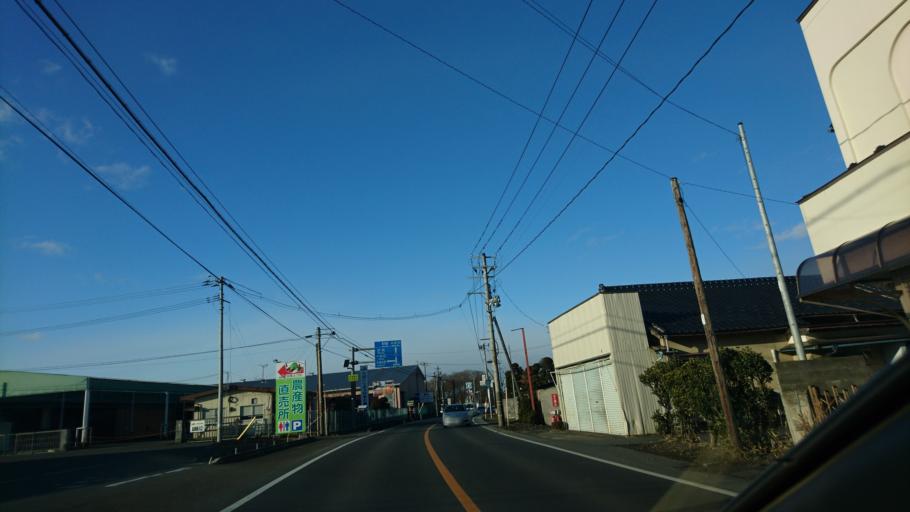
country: JP
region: Miyagi
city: Furukawa
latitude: 38.5169
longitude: 140.8628
